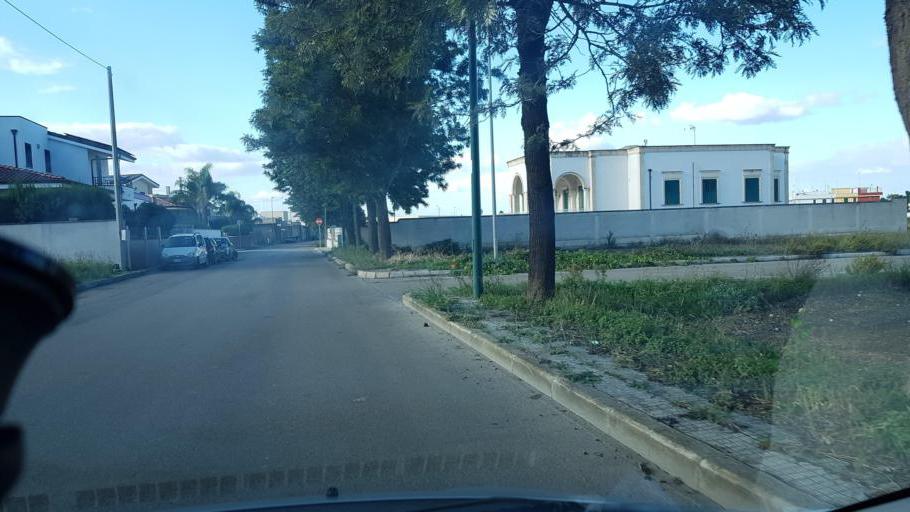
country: IT
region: Apulia
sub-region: Provincia di Lecce
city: Guagnano
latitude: 40.3990
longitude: 17.9565
